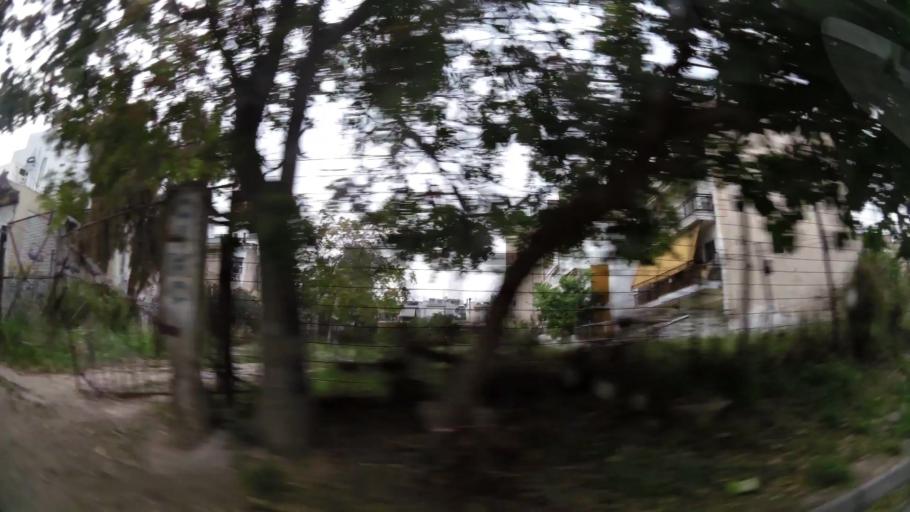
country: GR
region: Attica
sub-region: Nomarchia Athinas
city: Moskhaton
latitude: 37.9562
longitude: 23.6725
